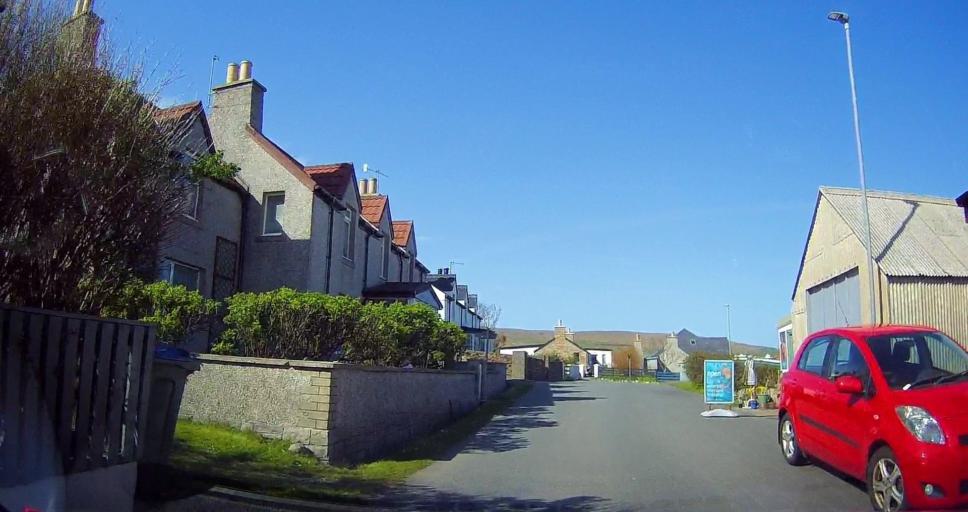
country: GB
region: Scotland
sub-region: Shetland Islands
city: Sandwick
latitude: 59.9981
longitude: -1.2549
